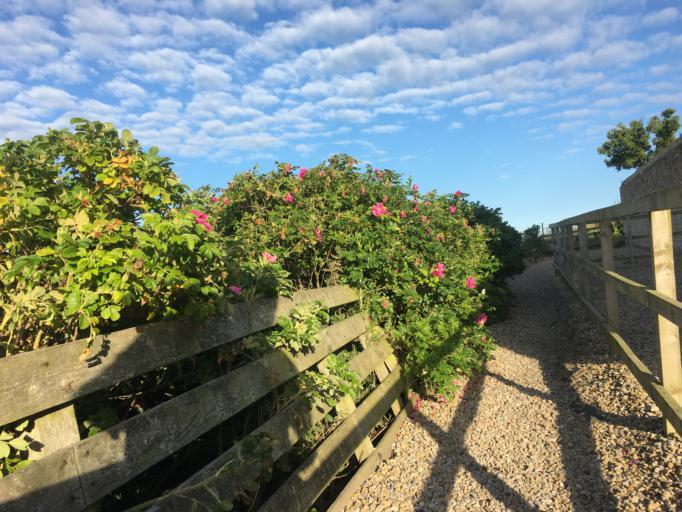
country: GB
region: England
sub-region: Northumberland
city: Bamburgh
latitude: 55.6021
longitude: -1.7002
